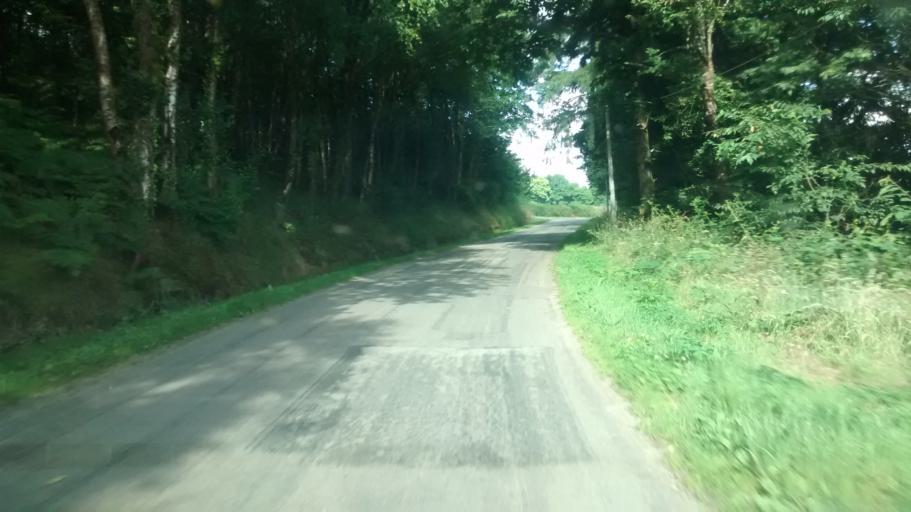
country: FR
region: Brittany
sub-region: Departement du Morbihan
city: Molac
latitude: 47.7198
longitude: -2.4709
